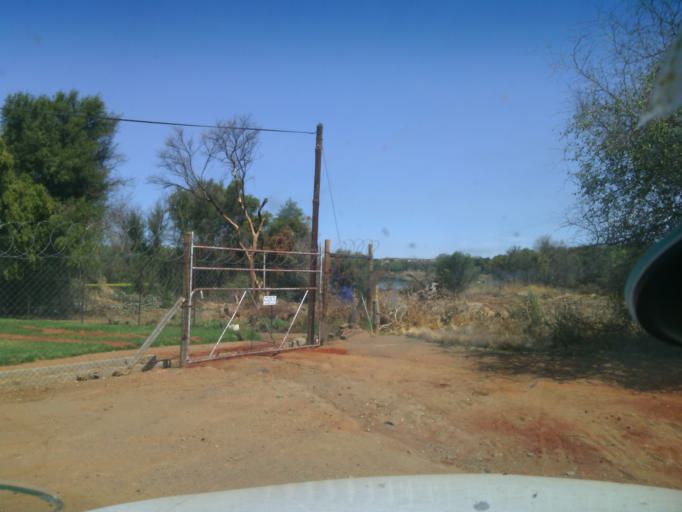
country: ZA
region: Northern Cape
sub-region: Frances Baard District Municipality
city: Barkly West
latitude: -28.5389
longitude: 24.5245
